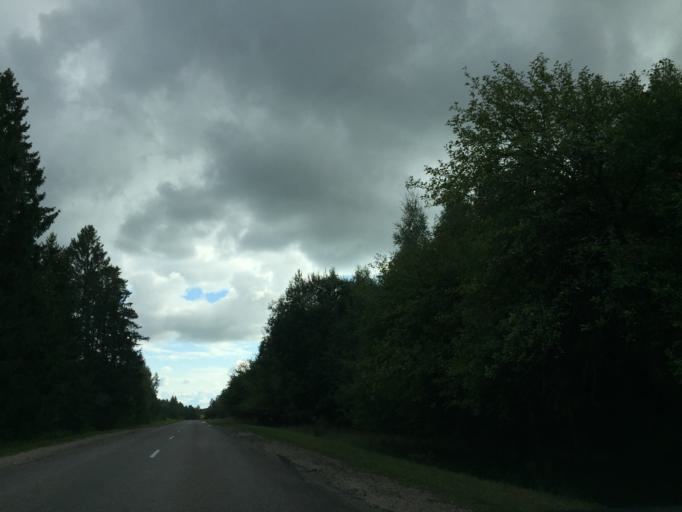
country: LV
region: Limbazu Rajons
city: Limbazi
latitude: 57.3610
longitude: 24.6701
